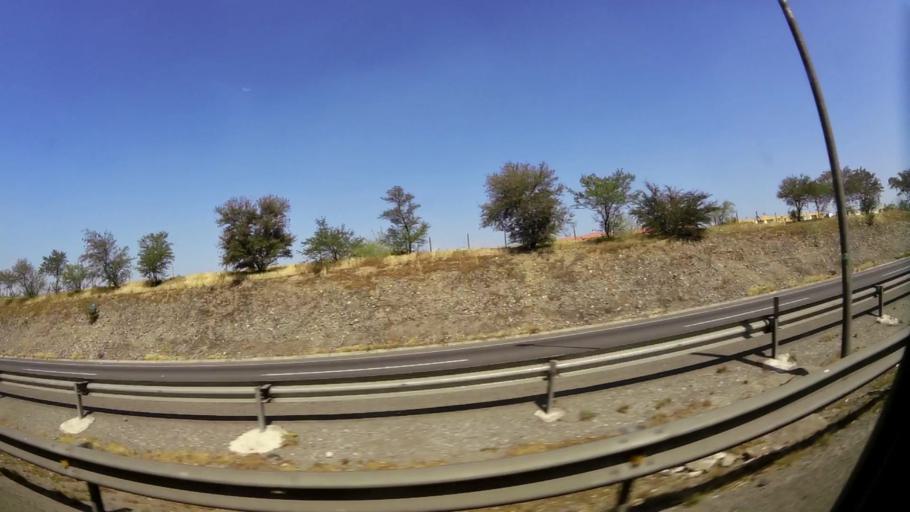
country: CL
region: Santiago Metropolitan
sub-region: Provincia de Santiago
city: Lo Prado
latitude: -33.4841
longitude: -70.7357
